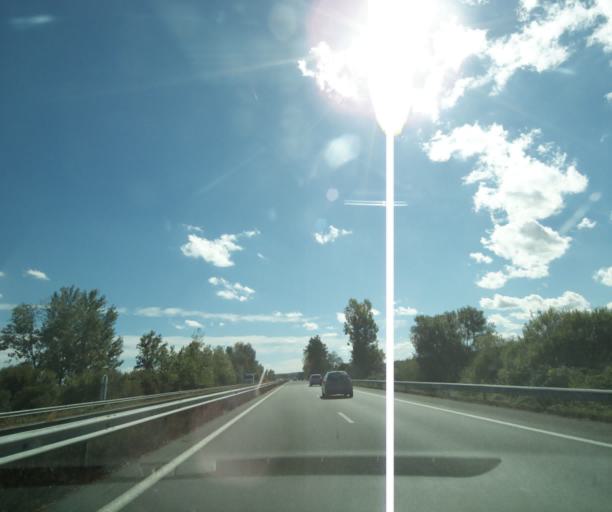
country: FR
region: Aquitaine
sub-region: Departement du Lot-et-Garonne
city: Damazan
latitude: 44.3163
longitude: 0.2596
